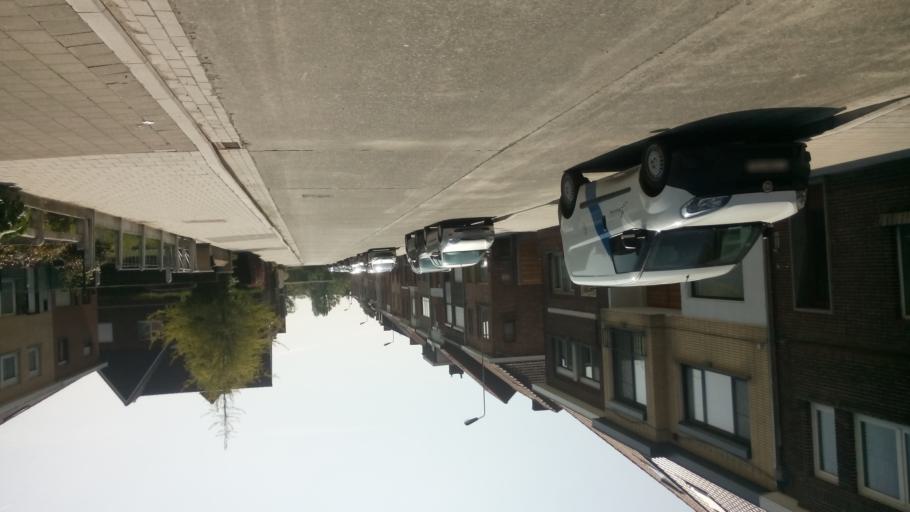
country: BE
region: Flanders
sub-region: Provincie Oost-Vlaanderen
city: Sint-Martens-Latem
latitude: 51.0545
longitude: 3.6568
